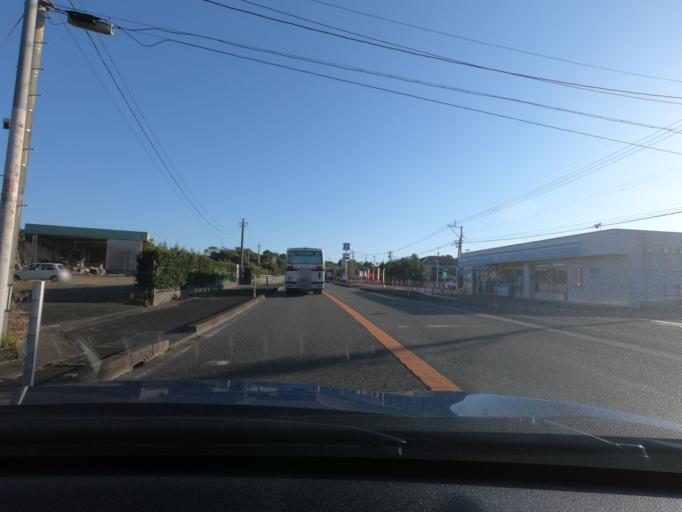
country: JP
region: Kagoshima
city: Akune
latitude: 31.9803
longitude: 130.2034
